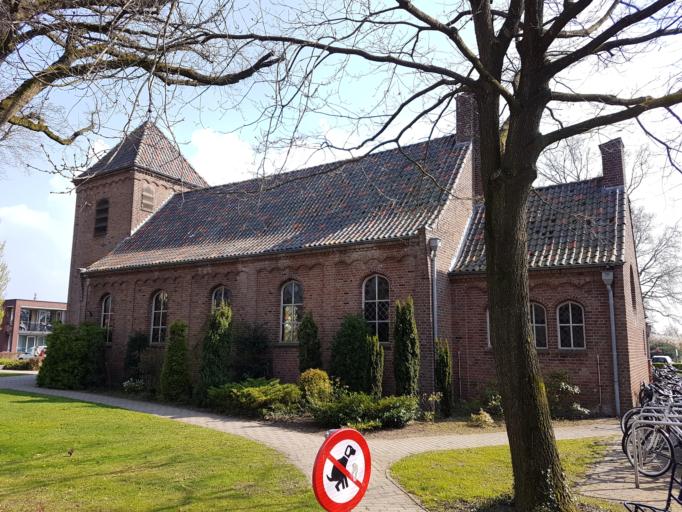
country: NL
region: Overijssel
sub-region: Gemeente Dalfsen
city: Dalfsen
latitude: 52.5326
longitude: 6.3111
